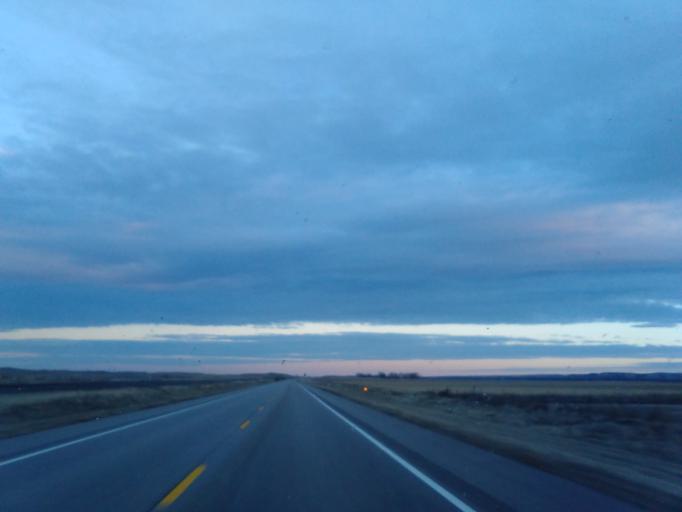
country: US
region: Nebraska
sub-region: Garden County
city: Oshkosh
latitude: 41.3848
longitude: -102.2821
